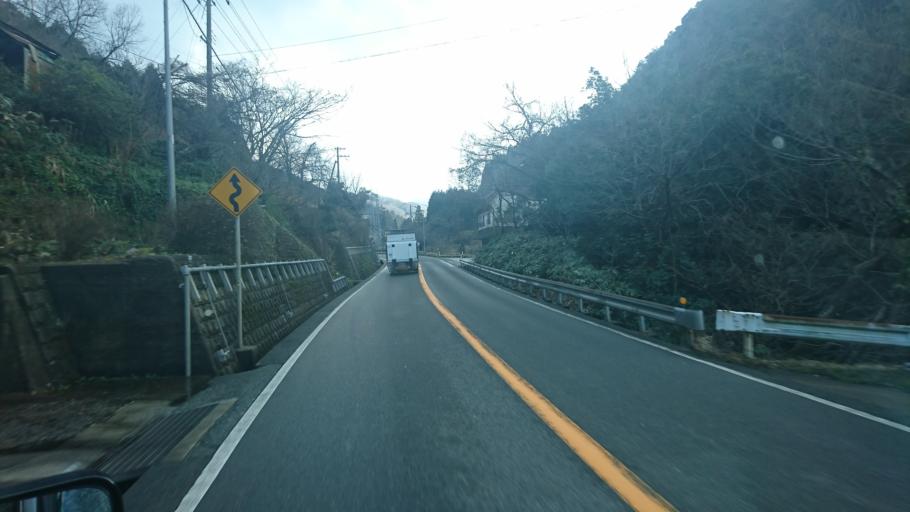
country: JP
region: Tottori
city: Tottori
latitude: 35.5443
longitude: 134.5042
